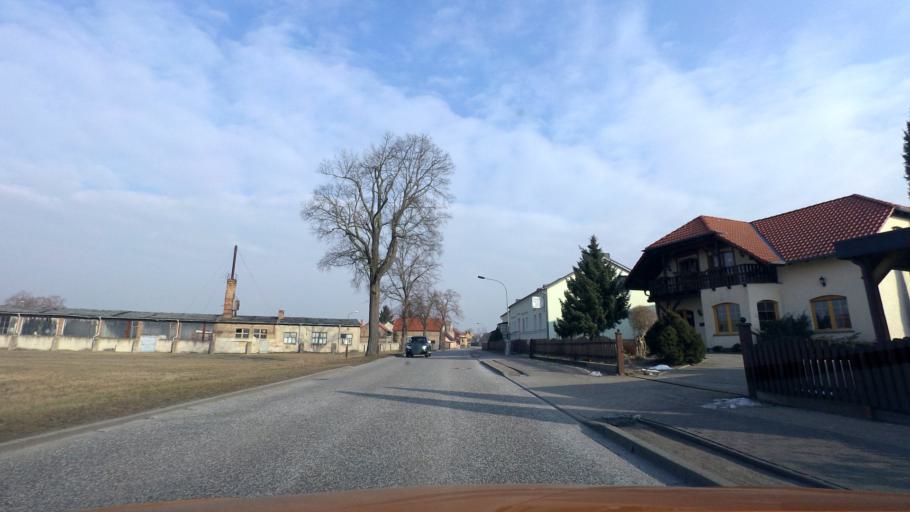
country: DE
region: Brandenburg
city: Trebbin
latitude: 52.2269
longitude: 13.3128
